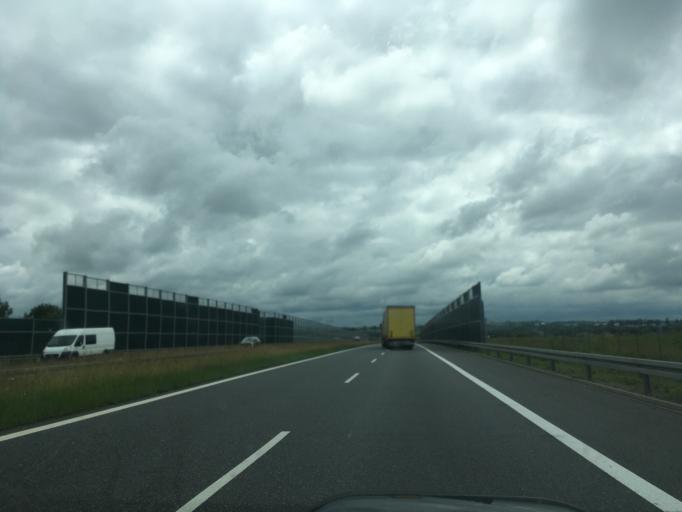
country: PL
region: Lublin Voivodeship
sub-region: Powiat lubelski
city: Jakubowice Murowane
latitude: 51.2645
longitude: 22.6565
